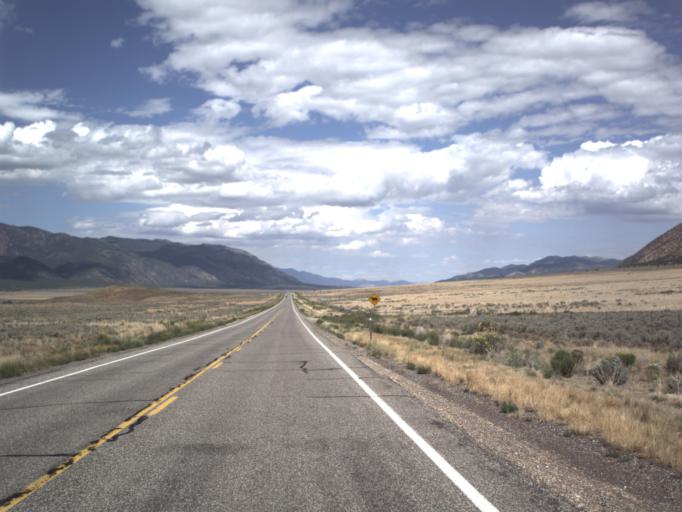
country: US
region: Utah
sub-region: Sevier County
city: Aurora
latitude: 39.0106
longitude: -112.0300
